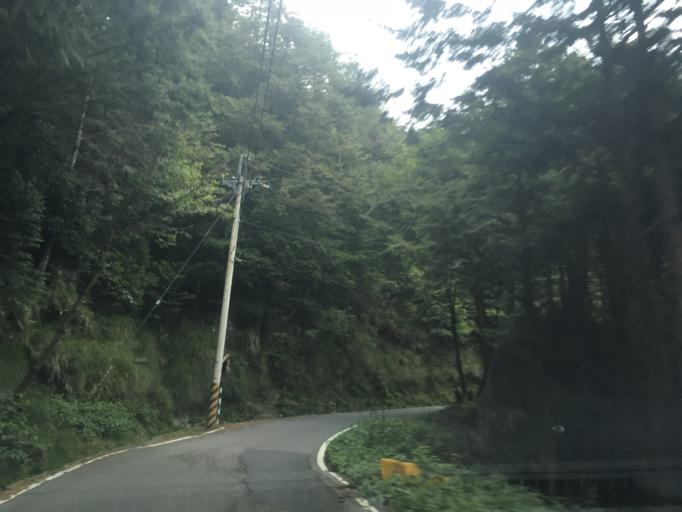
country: TW
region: Taiwan
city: Fengyuan
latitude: 24.2618
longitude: 121.0153
